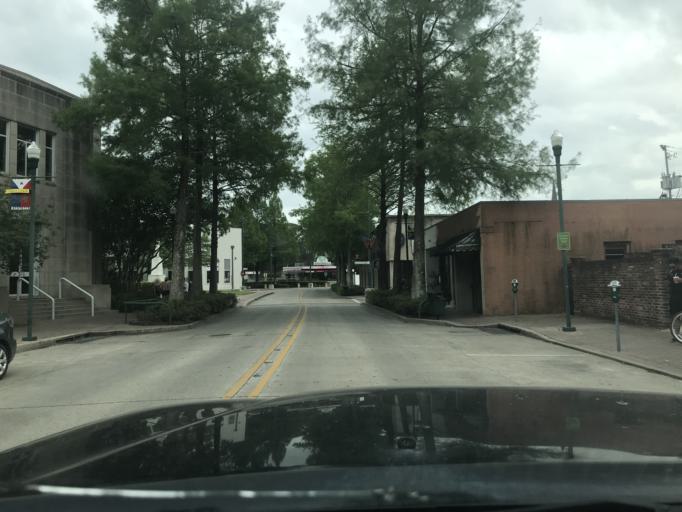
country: US
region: Louisiana
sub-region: Lafayette Parish
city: Lafayette
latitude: 30.2221
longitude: -92.0188
